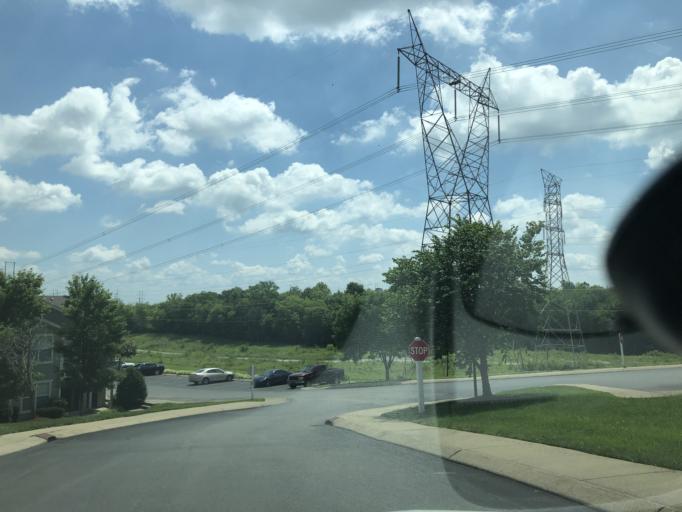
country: US
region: Tennessee
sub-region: Rutherford County
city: La Vergne
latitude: 36.0430
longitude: -86.6122
